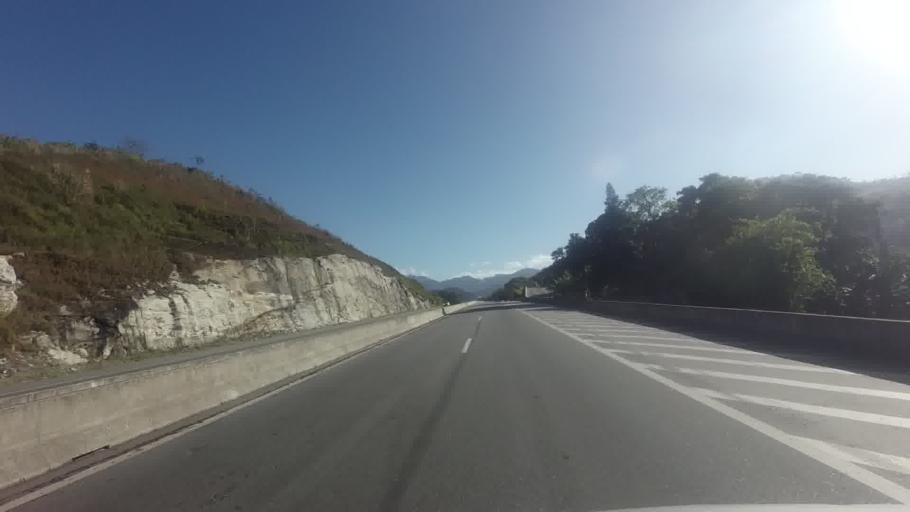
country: BR
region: Rio de Janeiro
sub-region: Petropolis
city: Petropolis
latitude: -22.6043
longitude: -43.2846
